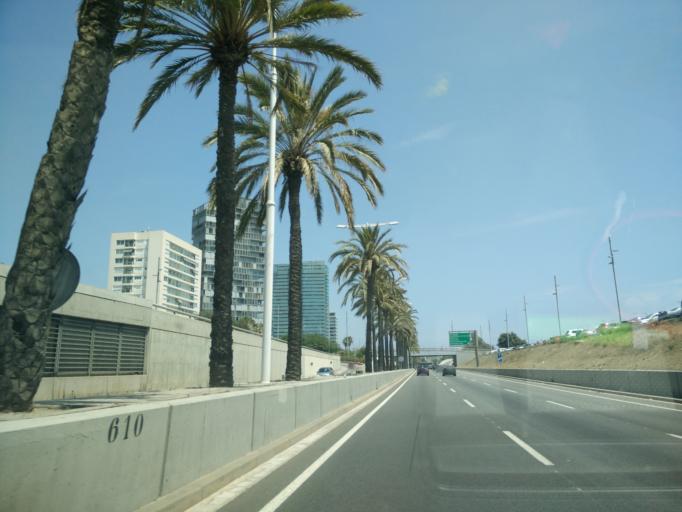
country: ES
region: Catalonia
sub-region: Provincia de Barcelona
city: Sant Marti
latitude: 41.4026
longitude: 2.2135
